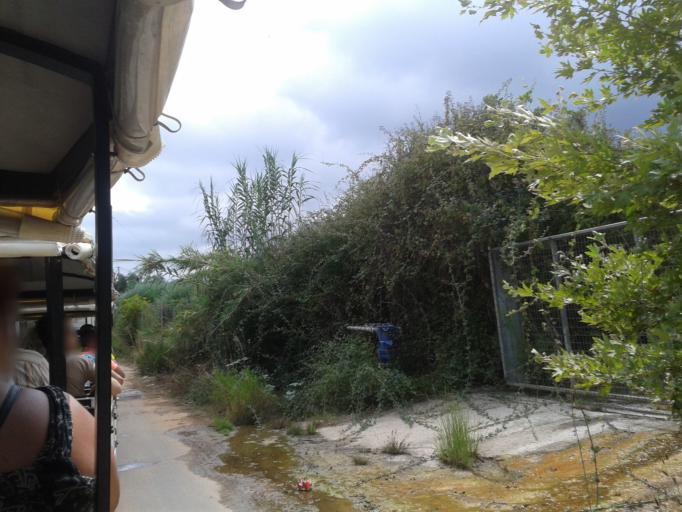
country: GR
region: Crete
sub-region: Nomos Chanias
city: Perivolia
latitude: 35.4863
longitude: 23.9815
